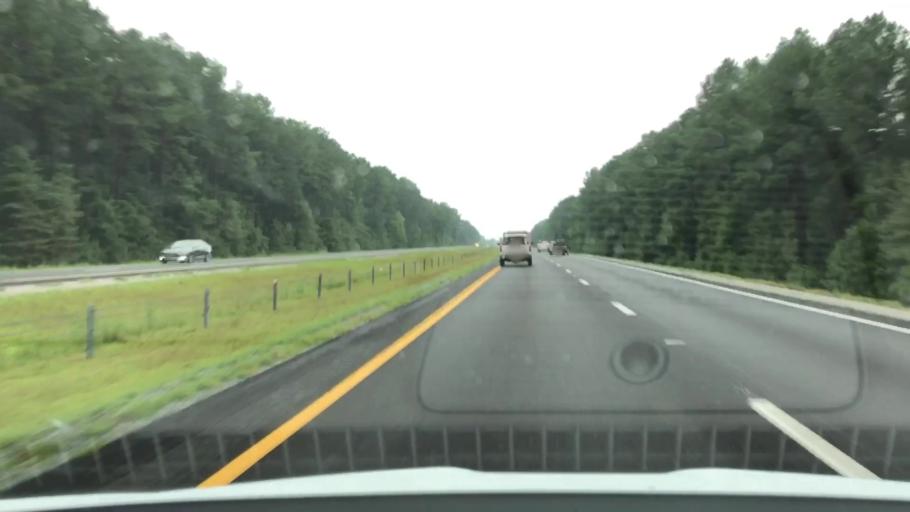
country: US
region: North Carolina
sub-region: Wayne County
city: Fremont
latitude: 35.4802
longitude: -77.9890
